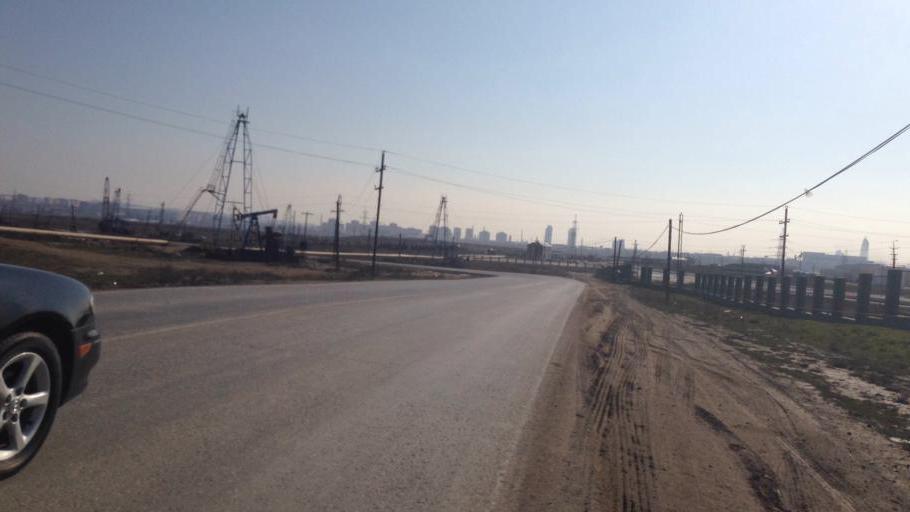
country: AZ
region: Baki
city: Balakhani
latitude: 40.4582
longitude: 49.8913
